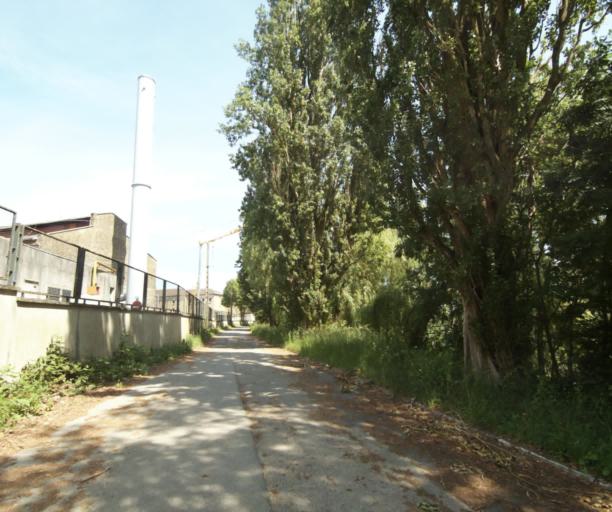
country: FR
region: Champagne-Ardenne
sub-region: Departement des Ardennes
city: Prix-les-Mezieres
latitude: 49.7617
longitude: 4.6966
